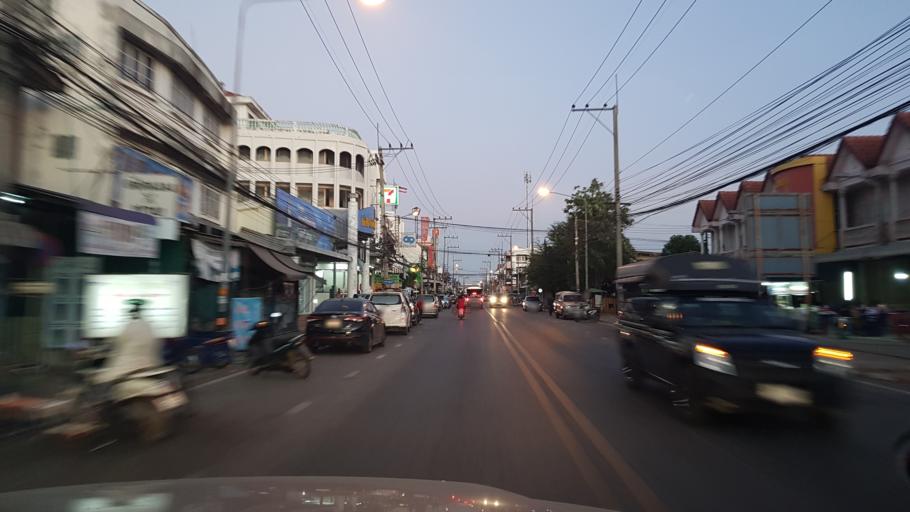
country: TH
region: Chaiyaphum
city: Phu Khiao
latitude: 16.3664
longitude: 102.1339
